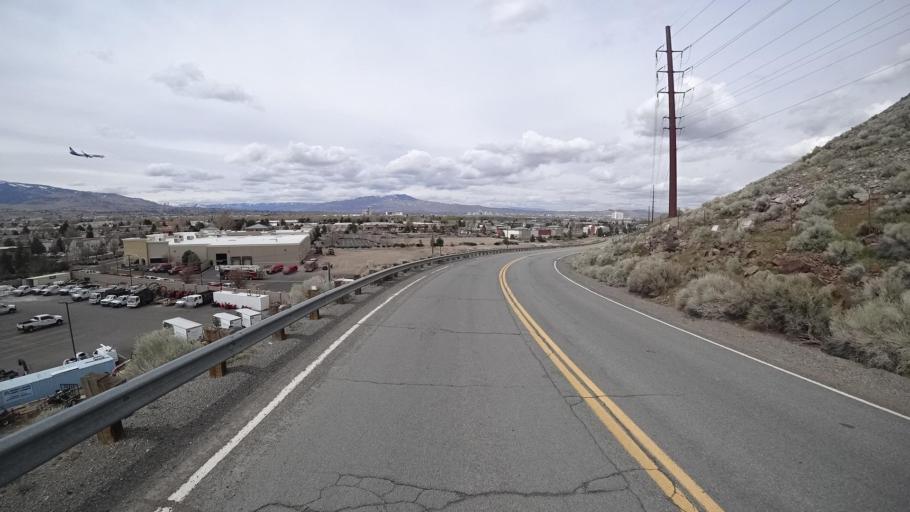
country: US
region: Nevada
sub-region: Washoe County
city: Sparks
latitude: 39.4709
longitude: -119.7624
